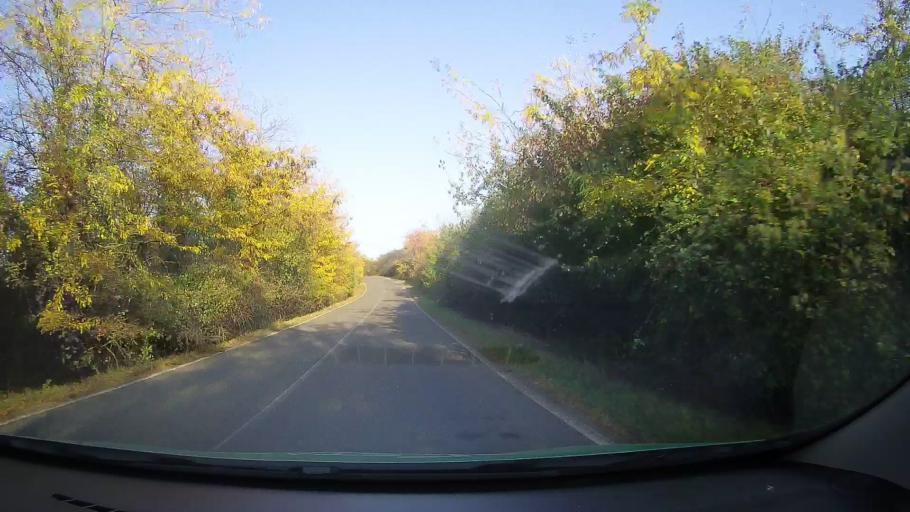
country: RO
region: Arad
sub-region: Comuna Tarnova
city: Chier
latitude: 46.3224
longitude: 21.8272
